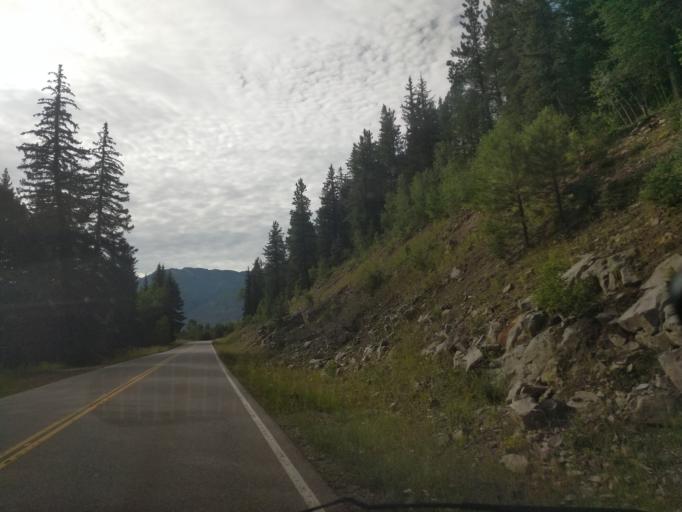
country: US
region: Colorado
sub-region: Garfield County
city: Carbondale
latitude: 39.0875
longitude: -107.2479
